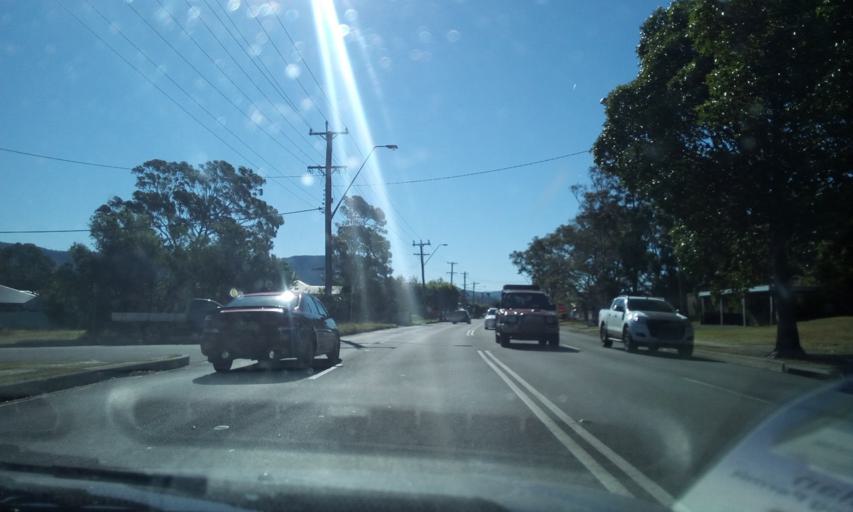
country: AU
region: New South Wales
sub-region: Wollongong
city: Dapto
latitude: -34.4999
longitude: 150.7903
